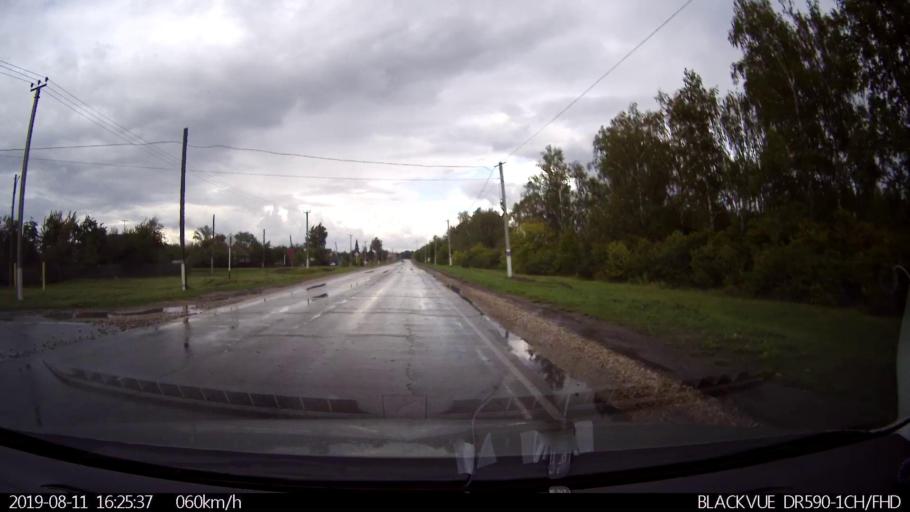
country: RU
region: Ulyanovsk
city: Mayna
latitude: 54.1064
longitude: 47.6064
